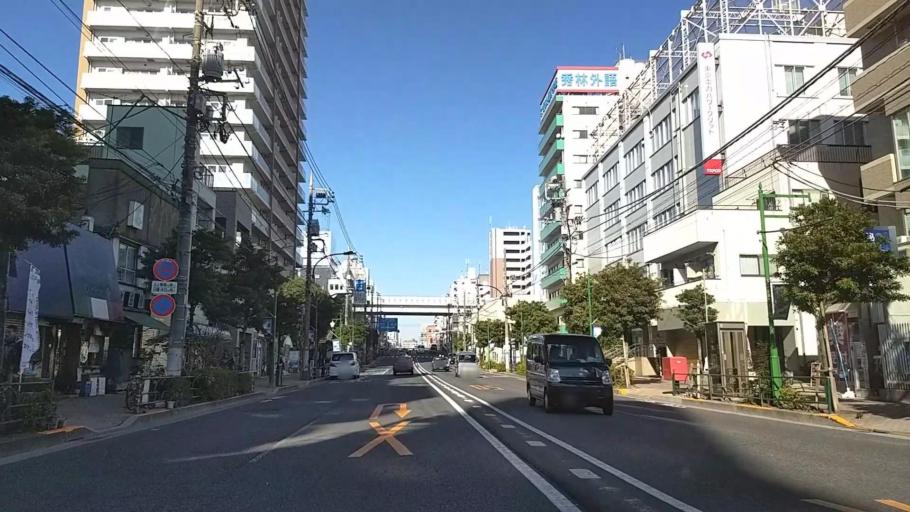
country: JP
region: Tokyo
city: Urayasu
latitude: 35.6920
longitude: 139.8261
